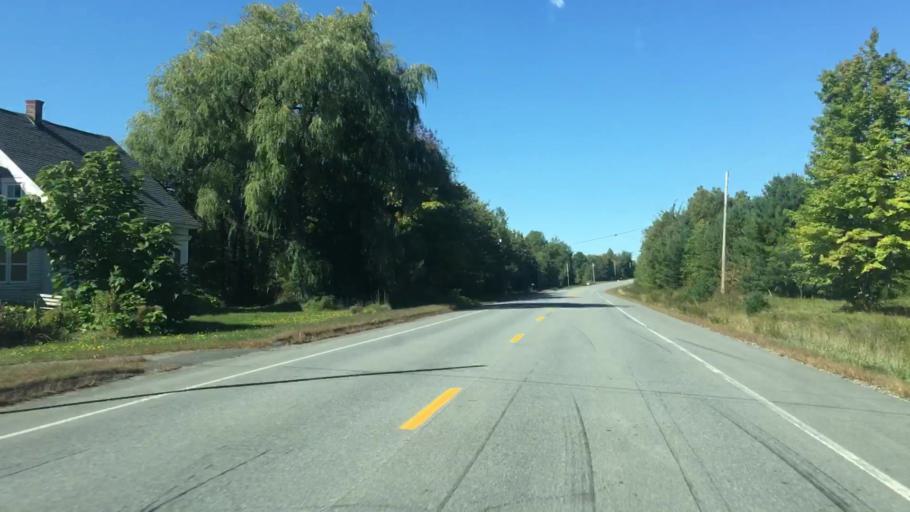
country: US
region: Maine
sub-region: Piscataquis County
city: Sangerville
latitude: 45.0674
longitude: -69.4587
